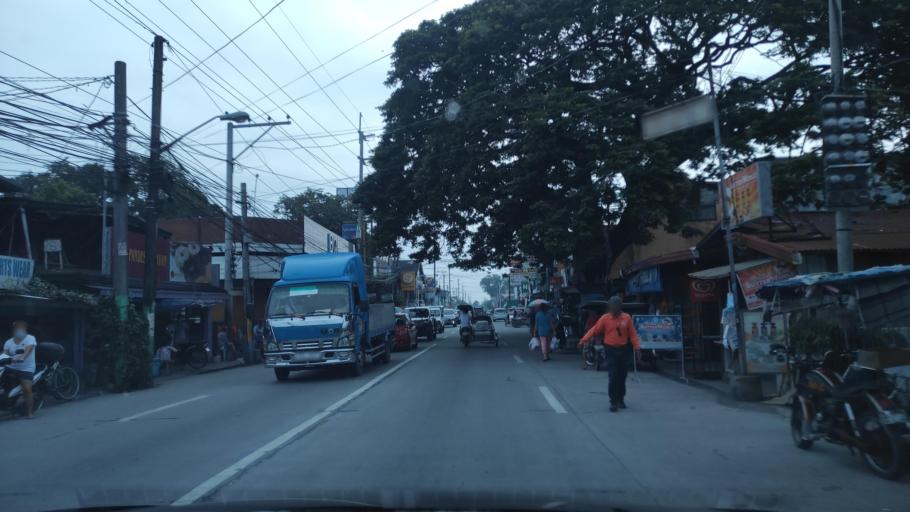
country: PH
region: Central Luzon
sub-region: Province of Pampanga
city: Santa Ana
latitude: 15.0950
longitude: 120.7665
